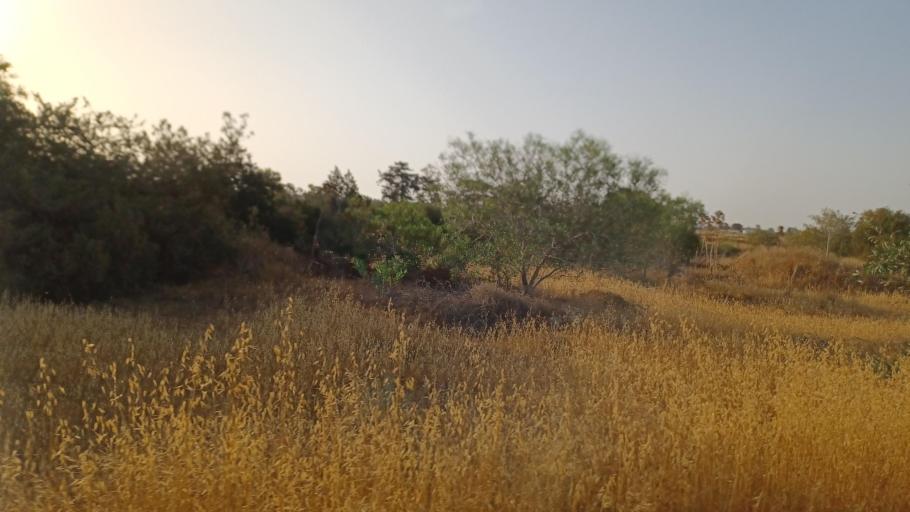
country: CY
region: Ammochostos
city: Liopetri
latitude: 34.9814
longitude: 33.8771
